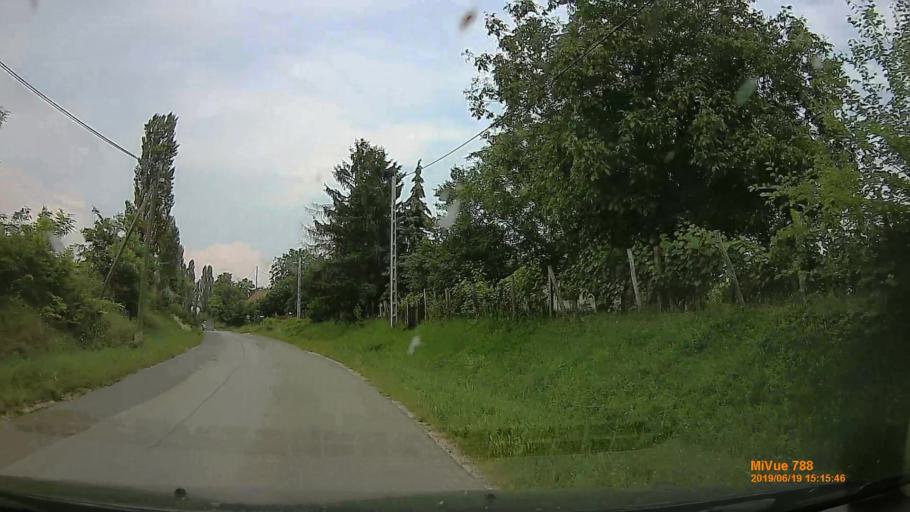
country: HU
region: Baranya
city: Szigetvar
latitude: 46.0744
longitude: 17.8363
